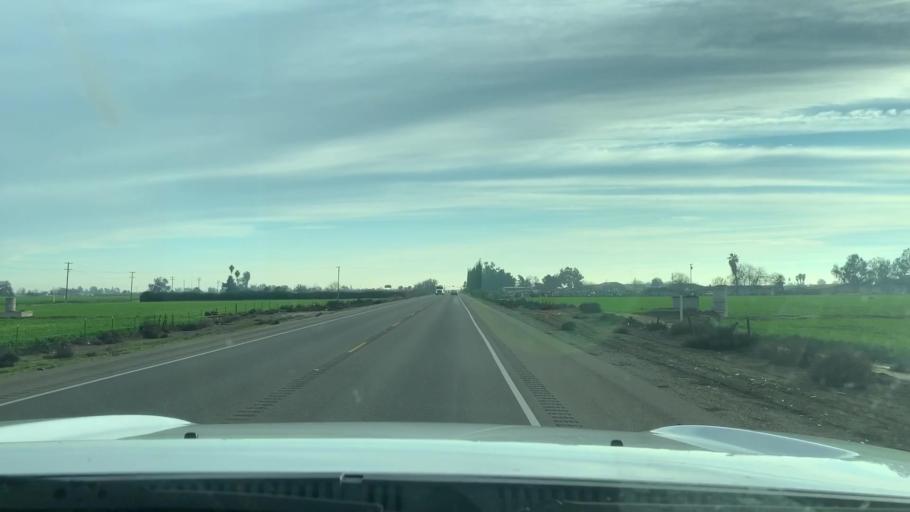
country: US
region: California
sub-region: Fresno County
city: Riverdale
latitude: 36.4407
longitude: -119.7992
